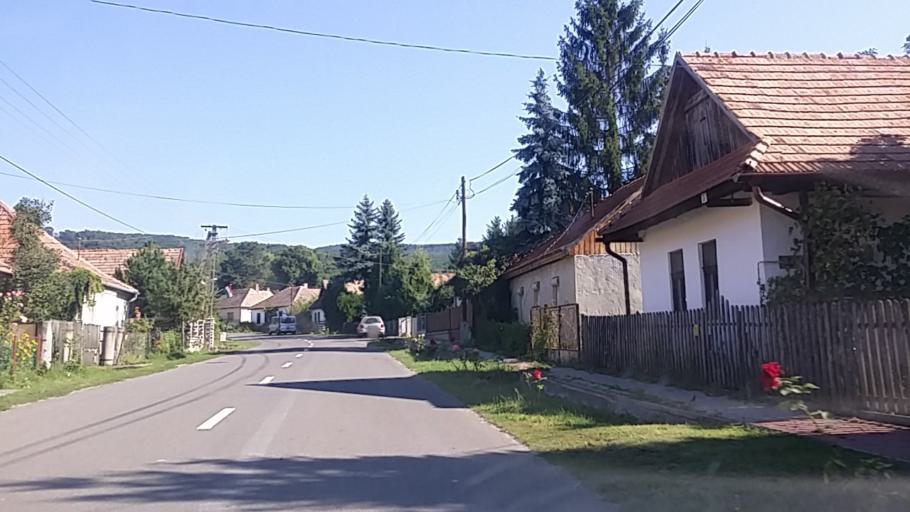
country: HU
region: Nograd
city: Paszto
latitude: 47.9157
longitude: 19.6199
